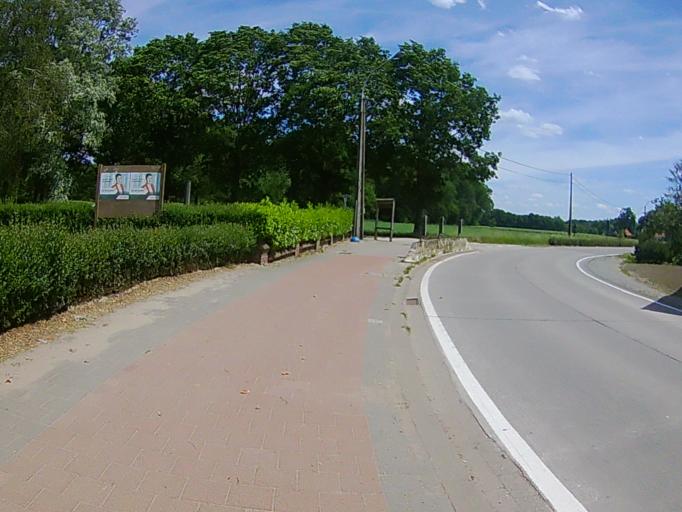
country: BE
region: Flanders
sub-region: Provincie Antwerpen
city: Grobbendonk
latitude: 51.1956
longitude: 4.7471
